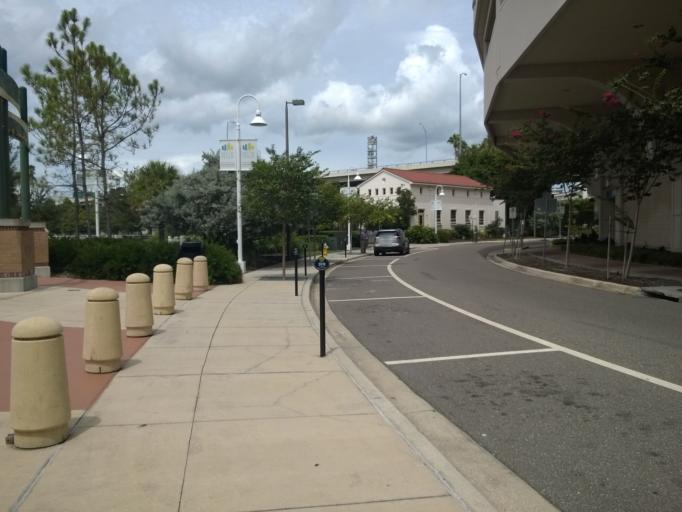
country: US
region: Florida
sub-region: Hillsborough County
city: Tampa
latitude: 27.9422
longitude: -82.4577
